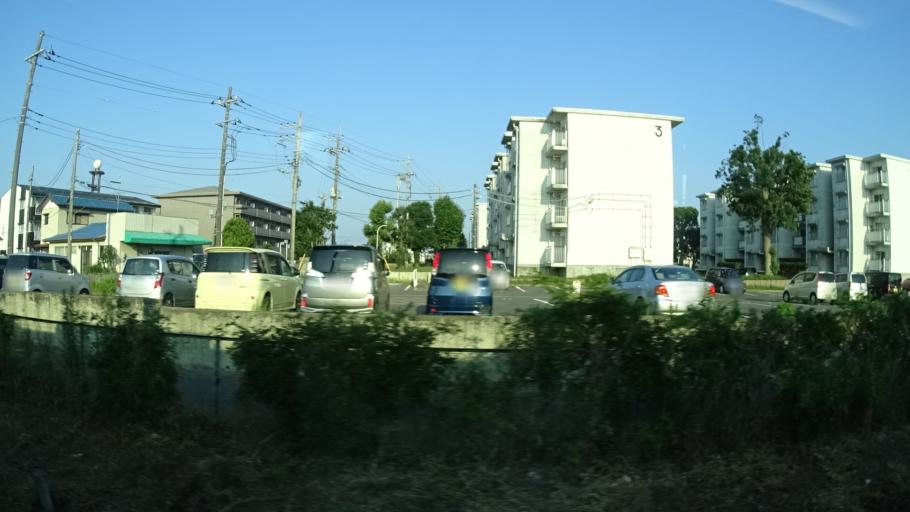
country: JP
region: Ibaraki
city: Hitachi-Naka
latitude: 36.4075
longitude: 140.5295
